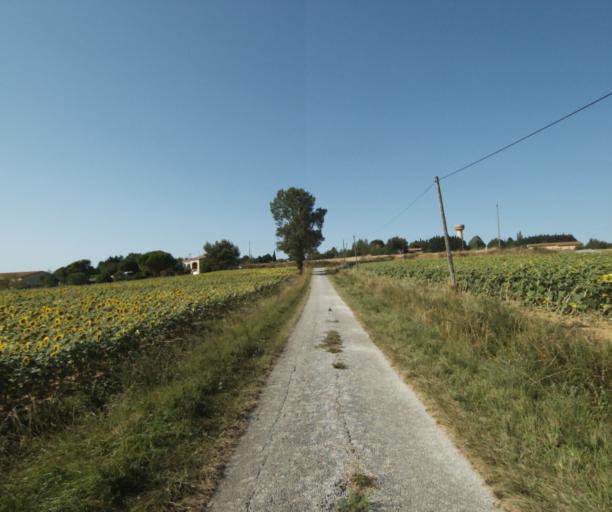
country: FR
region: Midi-Pyrenees
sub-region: Departement de la Haute-Garonne
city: Avignonet-Lauragais
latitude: 43.4227
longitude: 1.8173
